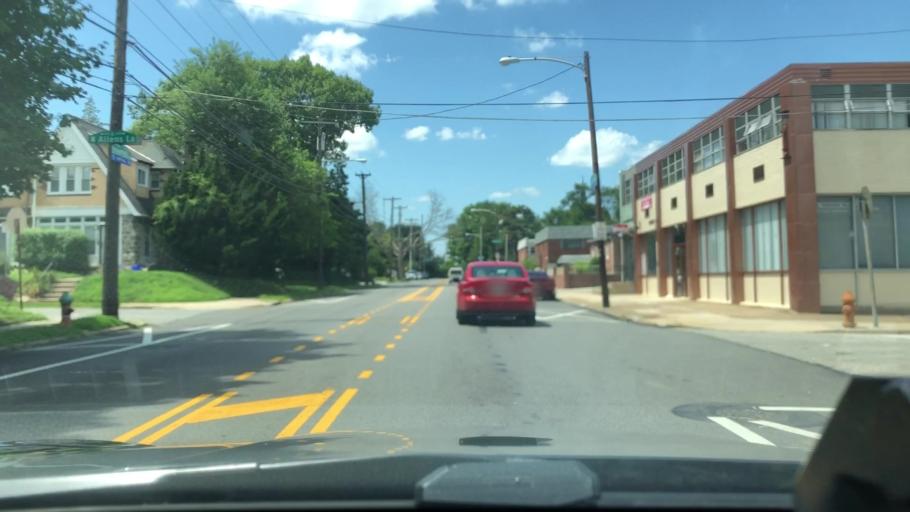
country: US
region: Pennsylvania
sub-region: Montgomery County
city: Wyndmoor
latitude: 40.0692
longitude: -75.1823
